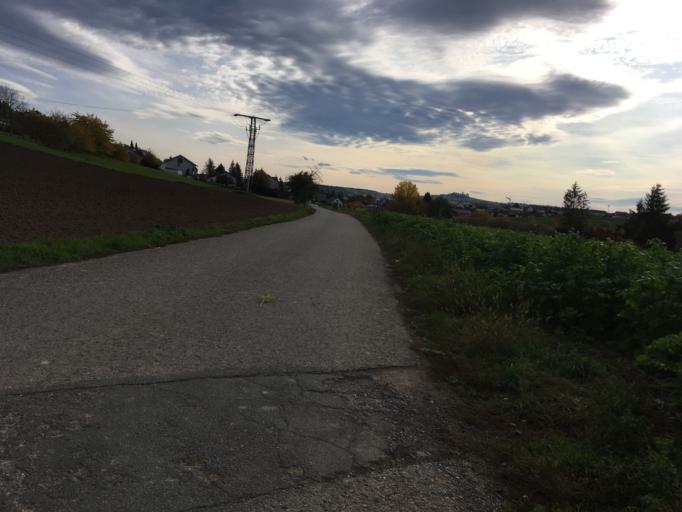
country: DE
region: Baden-Wuerttemberg
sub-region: Karlsruhe Region
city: Sinsheim
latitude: 49.2605
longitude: 8.9049
